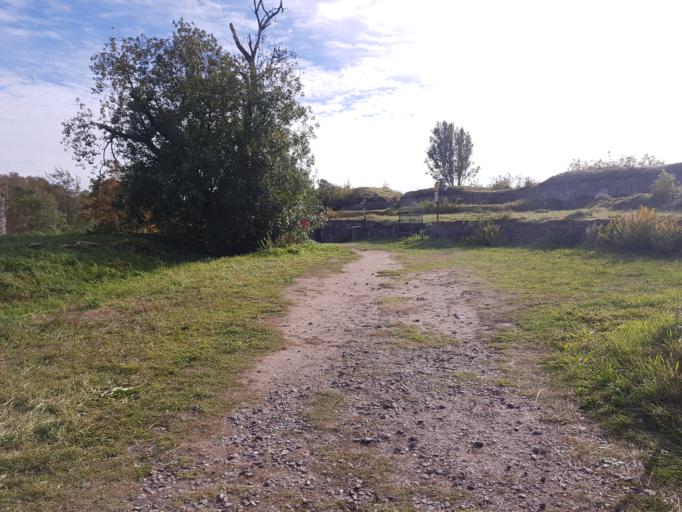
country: FI
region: Uusimaa
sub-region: Helsinki
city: Helsinki
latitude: 60.1363
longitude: 24.9961
